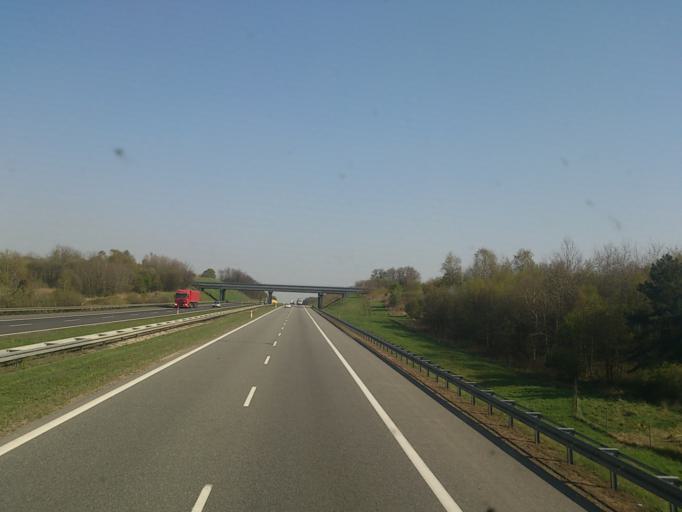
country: PL
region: Lesser Poland Voivodeship
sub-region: Powiat krakowski
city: Czulow
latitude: 50.0867
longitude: 19.6948
